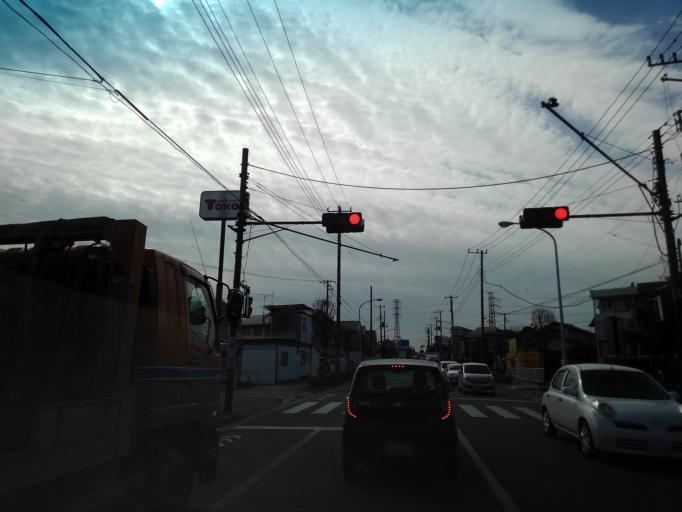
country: JP
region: Tokyo
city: Tanashicho
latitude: 35.7538
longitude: 139.5064
